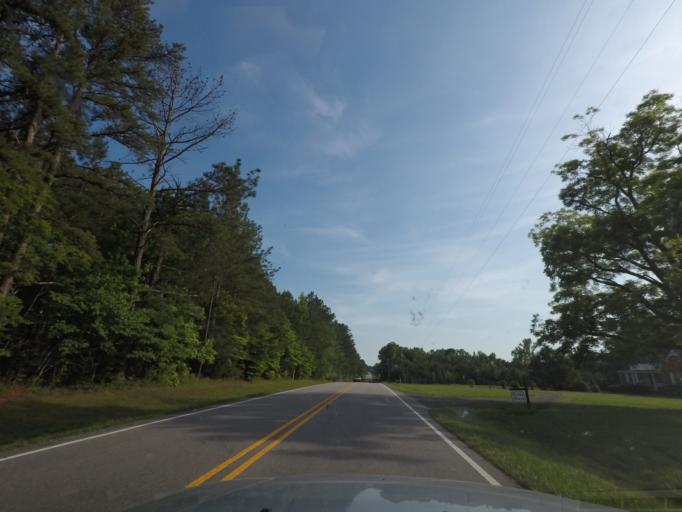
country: US
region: North Carolina
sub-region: Granville County
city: Oxford
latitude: 36.4621
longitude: -78.5620
